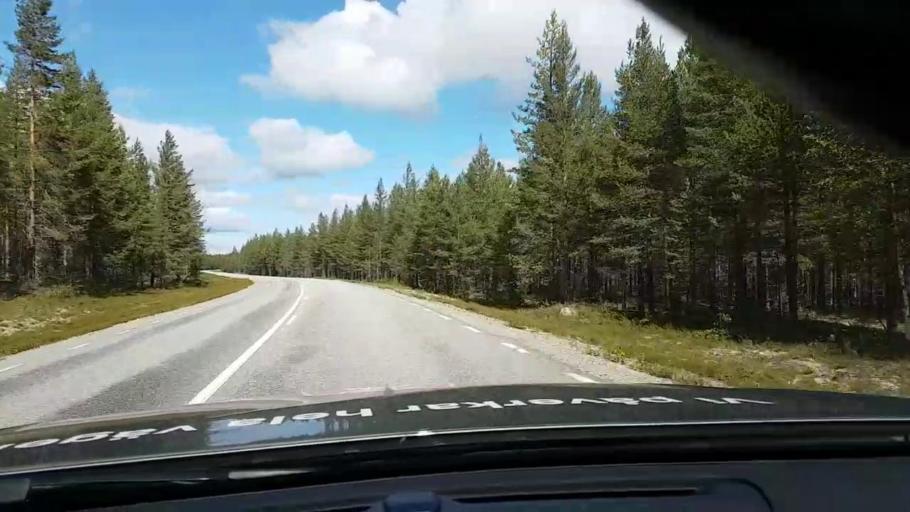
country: SE
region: Vaesternorrland
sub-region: OErnskoeldsviks Kommun
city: Bredbyn
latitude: 63.6163
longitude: 17.9068
